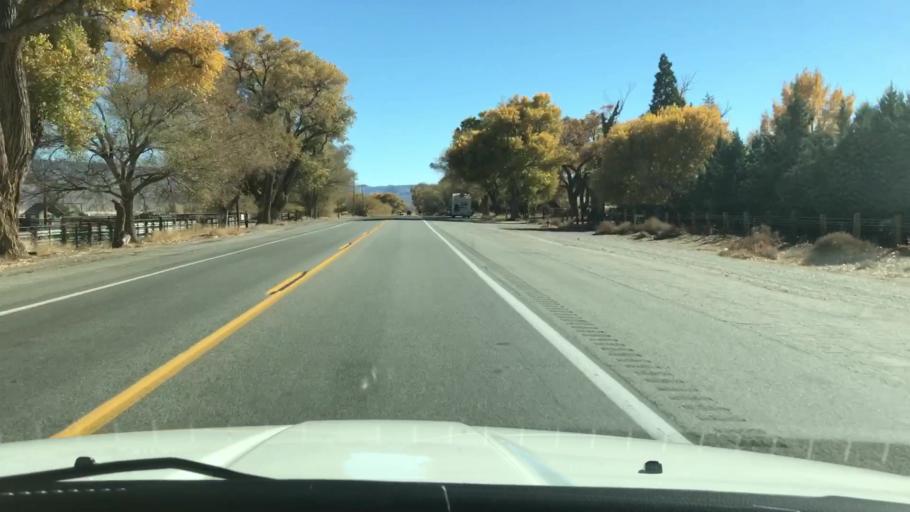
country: US
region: California
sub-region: Inyo County
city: Lone Pine
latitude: 36.2880
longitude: -118.0121
